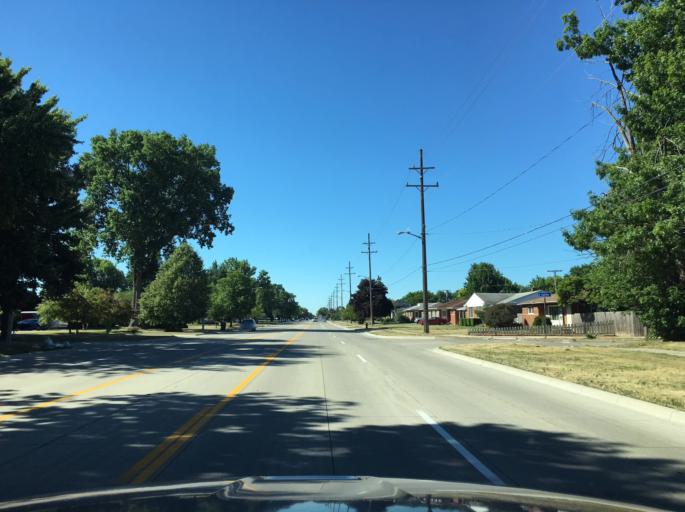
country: US
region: Michigan
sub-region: Macomb County
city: Saint Clair Shores
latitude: 42.5065
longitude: -82.9083
